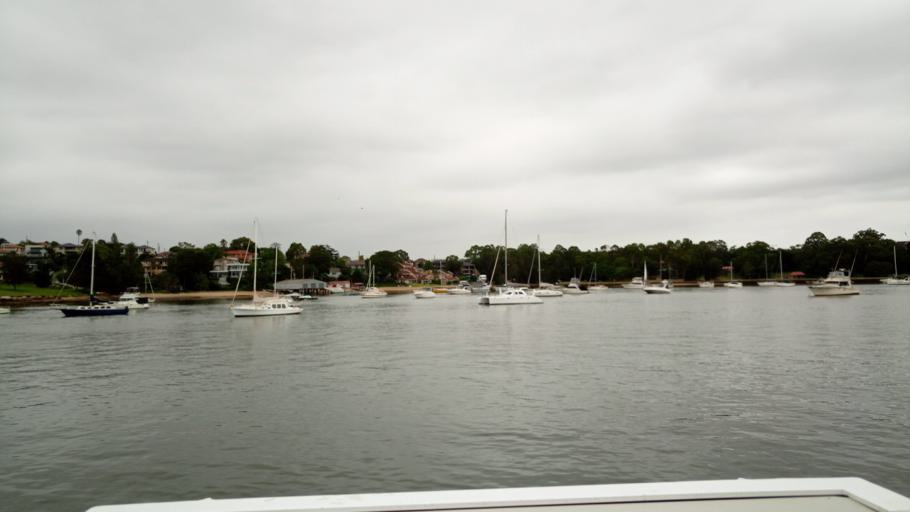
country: AU
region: New South Wales
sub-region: Canada Bay
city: Concord
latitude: -33.8332
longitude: 151.1039
